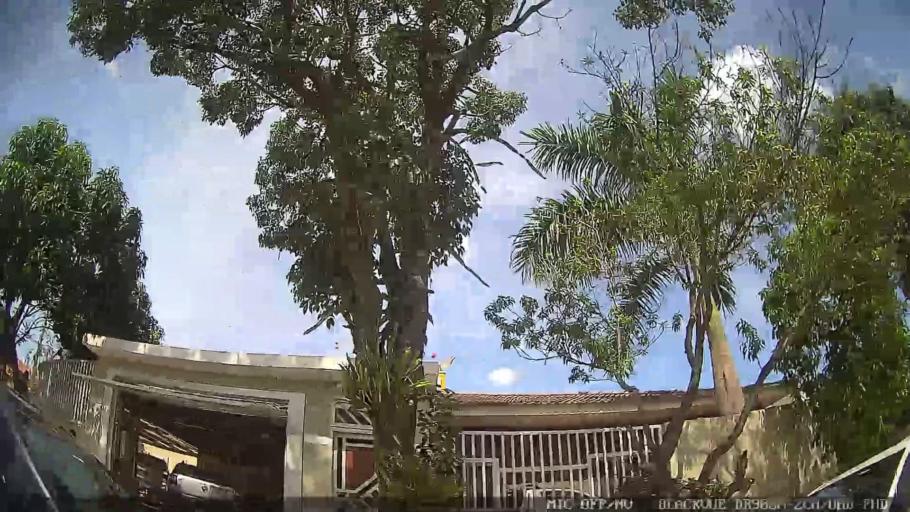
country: BR
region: Sao Paulo
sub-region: Artur Nogueira
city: Artur Nogueira
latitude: -22.6115
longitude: -47.0681
